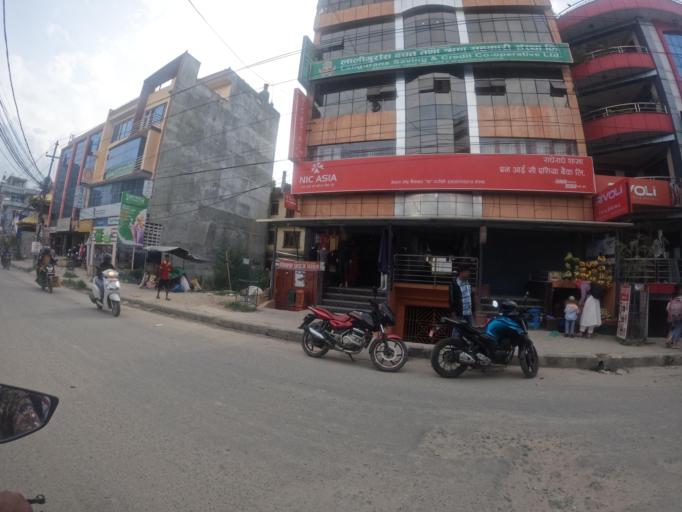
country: NP
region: Central Region
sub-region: Bagmati Zone
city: Bhaktapur
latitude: 27.6769
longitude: 85.3982
